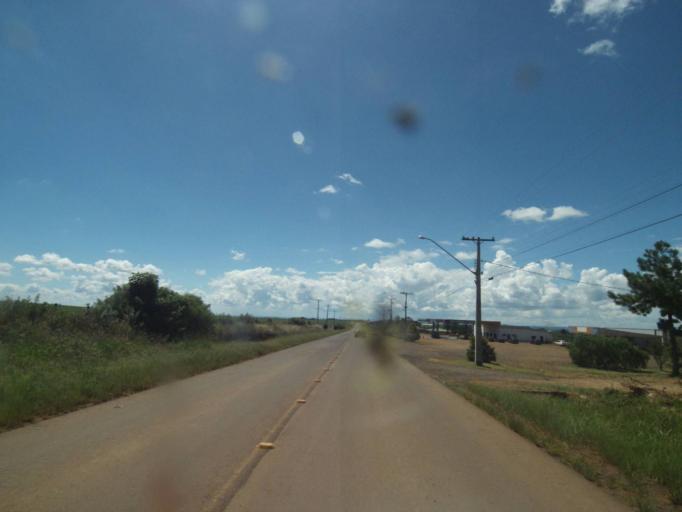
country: BR
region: Parana
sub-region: Pinhao
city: Pinhao
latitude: -25.8329
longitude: -52.0324
